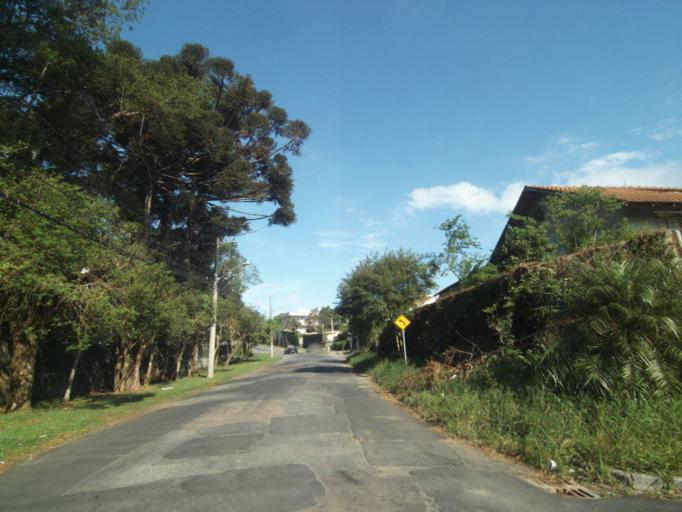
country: BR
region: Parana
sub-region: Curitiba
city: Curitiba
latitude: -25.3982
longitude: -49.2984
